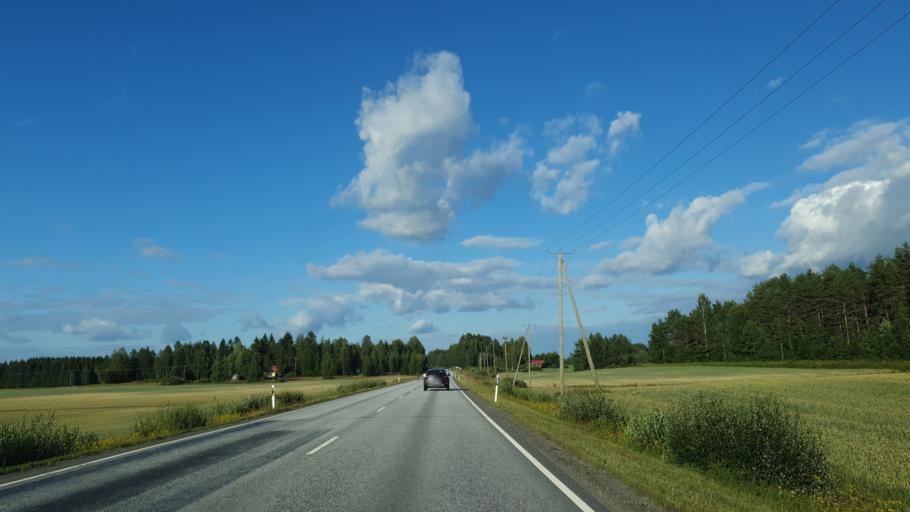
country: FI
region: North Karelia
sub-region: Joensuu
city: Liperi
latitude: 62.5719
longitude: 29.1645
